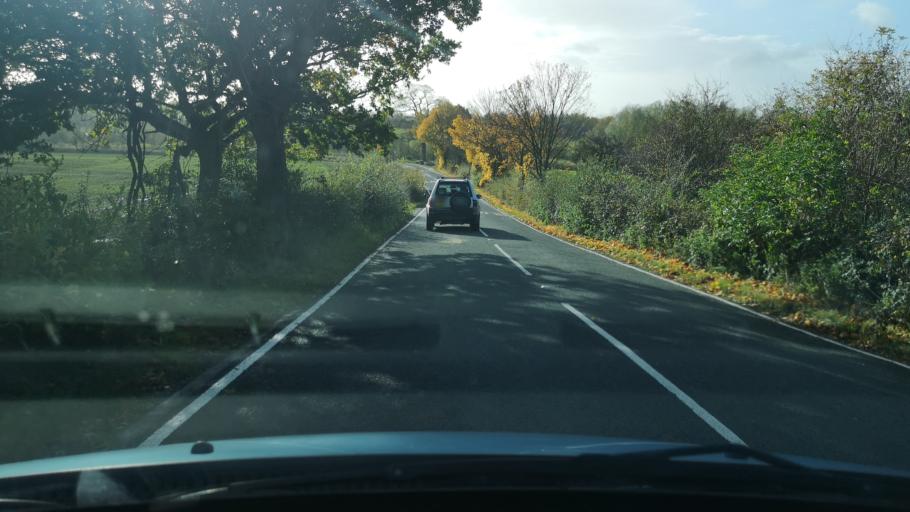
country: GB
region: England
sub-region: City and Borough of Wakefield
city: Crofton
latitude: 53.6458
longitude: -1.4199
